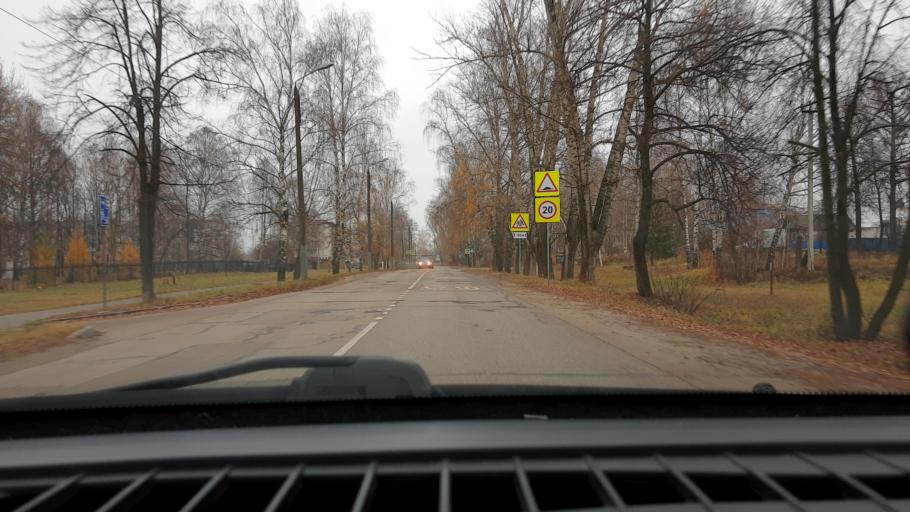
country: RU
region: Nizjnij Novgorod
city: Kstovo
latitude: 56.1812
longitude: 44.1596
